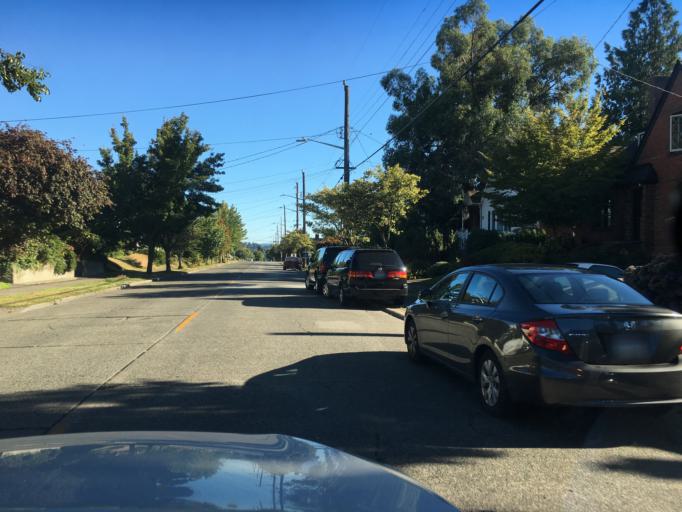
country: US
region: Washington
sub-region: King County
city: Shoreline
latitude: 47.6865
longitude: -122.3983
